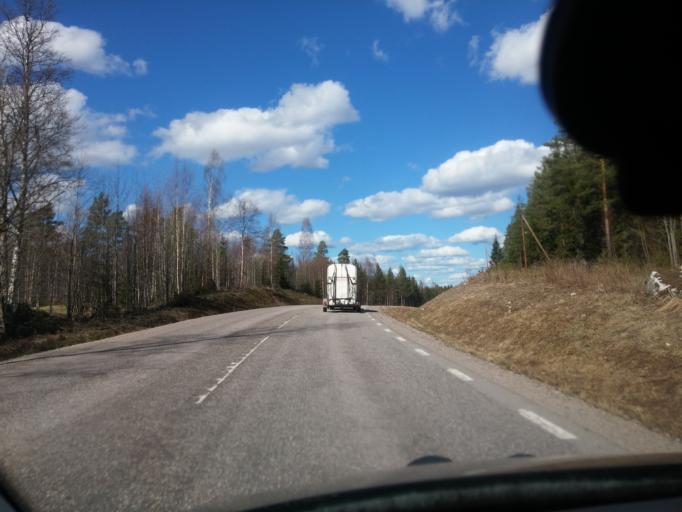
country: SE
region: Gaevleborg
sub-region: Ovanakers Kommun
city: Edsbyn
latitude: 61.2571
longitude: 15.8840
